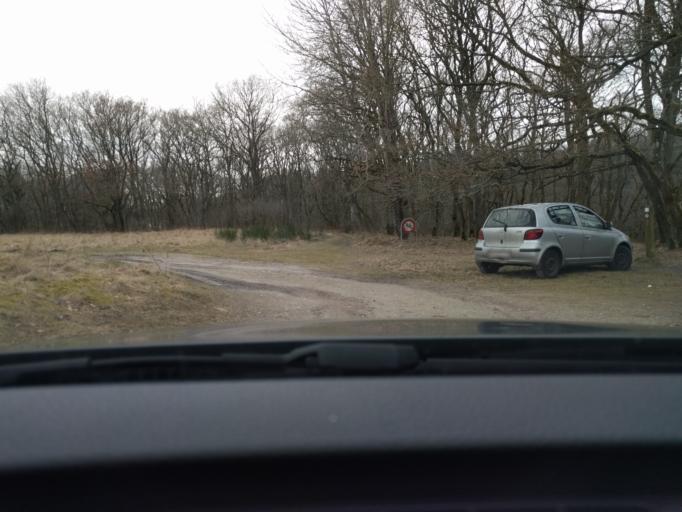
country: DK
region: Central Jutland
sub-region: Holstebro Kommune
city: Vinderup
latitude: 56.5012
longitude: 8.9005
